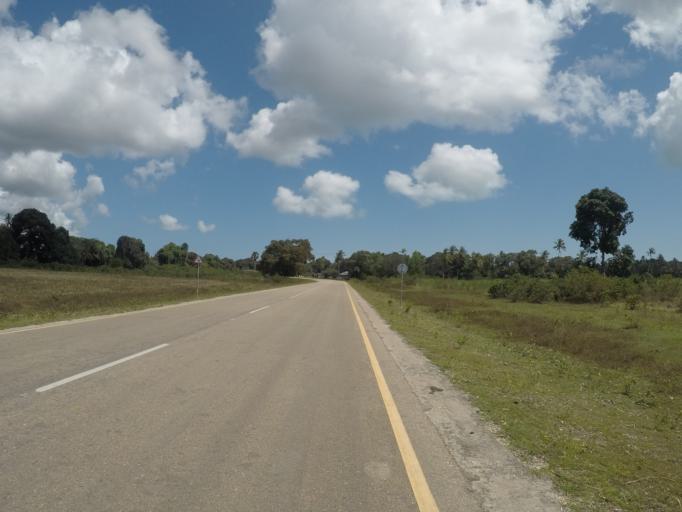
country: TZ
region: Zanzibar Central/South
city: Koani
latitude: -6.2298
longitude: 39.3598
